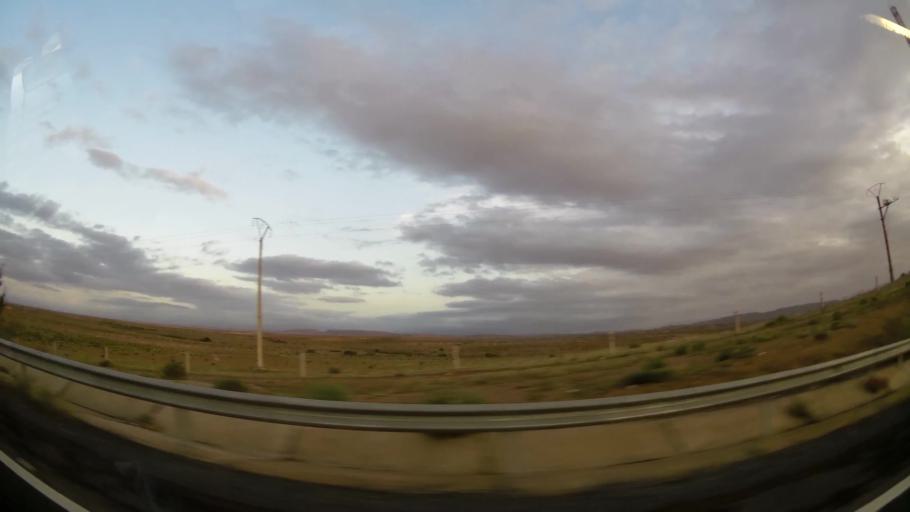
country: MA
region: Oriental
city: Taourirt
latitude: 34.5478
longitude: -2.8961
